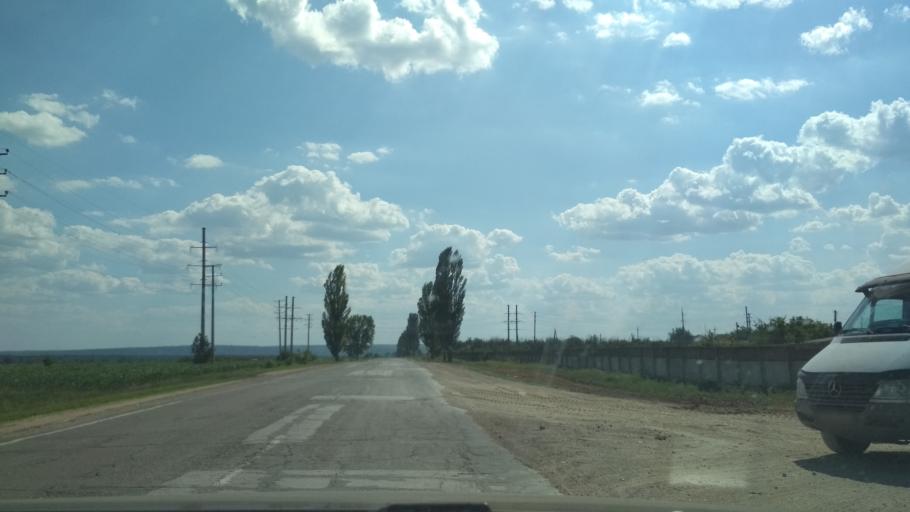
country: MD
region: Criuleni
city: Criuleni
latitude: 47.1483
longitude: 29.1482
